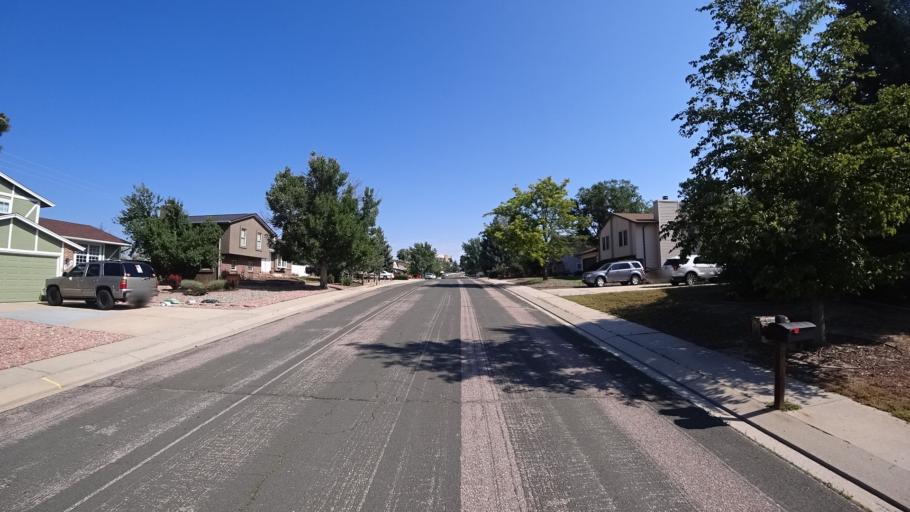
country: US
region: Colorado
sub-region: El Paso County
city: Air Force Academy
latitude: 38.9557
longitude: -104.7837
